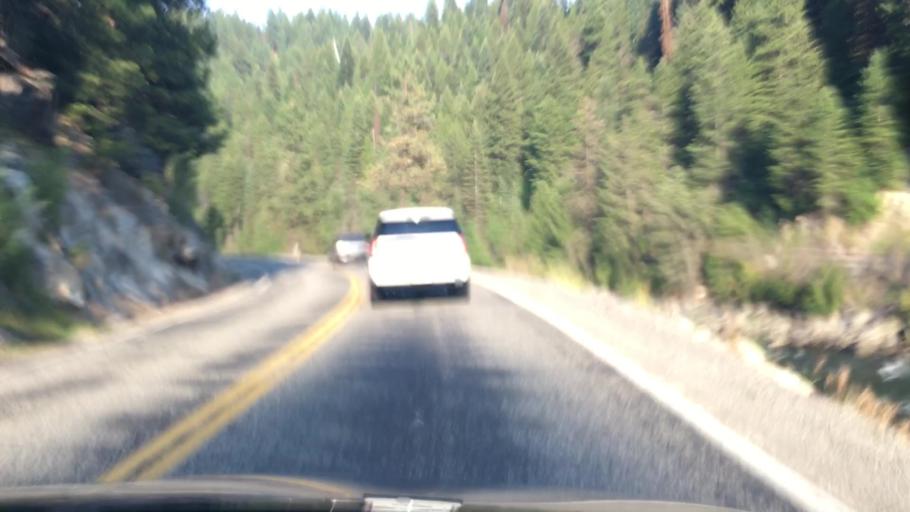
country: US
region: Idaho
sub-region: Valley County
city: Cascade
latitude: 44.3177
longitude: -116.0657
